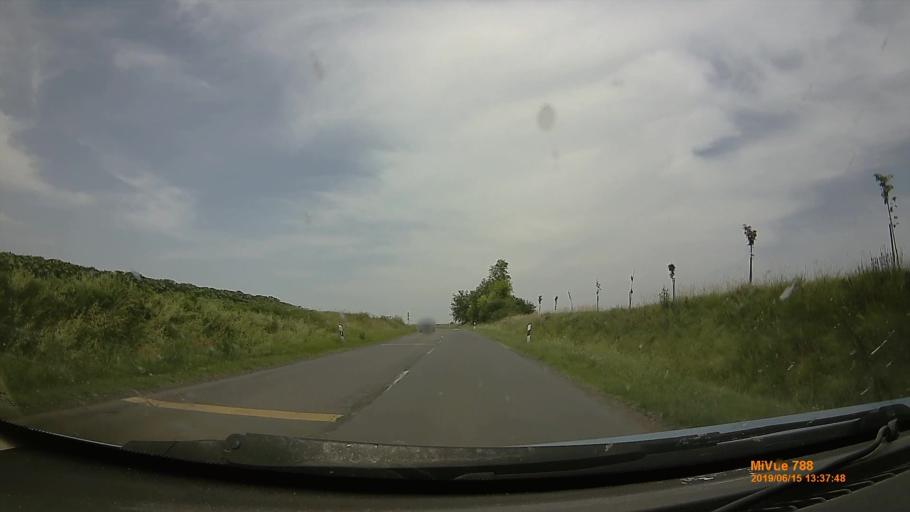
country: HU
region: Tolna
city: Tamasi
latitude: 46.6067
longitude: 18.2077
